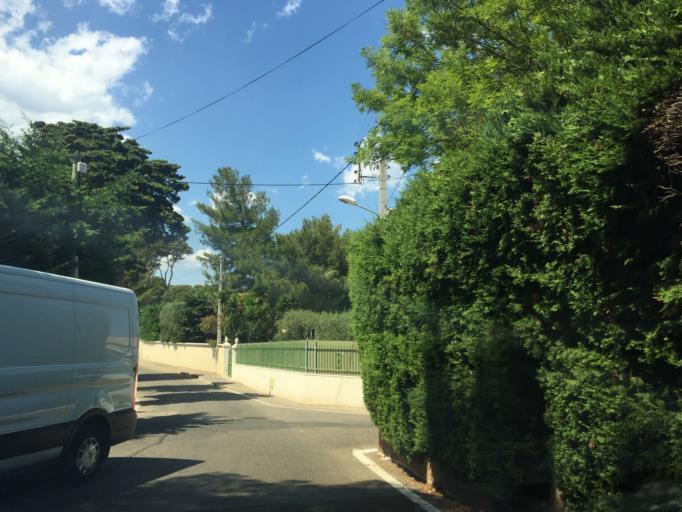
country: FR
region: Provence-Alpes-Cote d'Azur
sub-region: Departement des Alpes-Maritimes
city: Antibes
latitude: 43.5535
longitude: 7.1335
